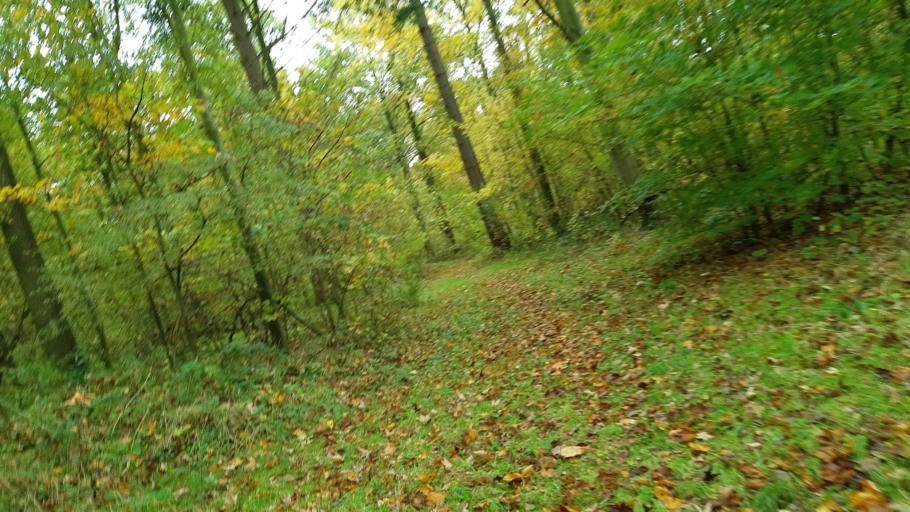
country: NL
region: Friesland
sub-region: Gemeente Lemsterland
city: Echtenerbrug
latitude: 52.7767
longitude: 5.8188
